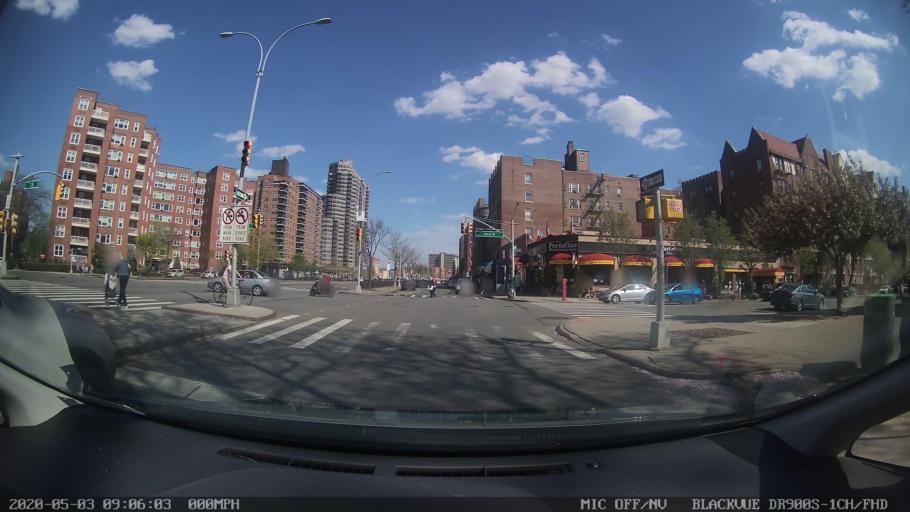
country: US
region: New York
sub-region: Queens County
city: Borough of Queens
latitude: 40.7196
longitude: -73.8401
